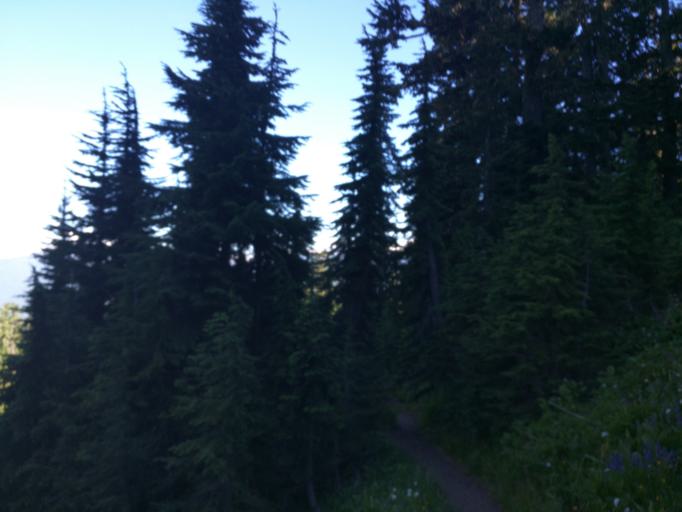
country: CA
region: British Columbia
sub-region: Fraser Valley Regional District
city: Chilliwack
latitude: 48.9263
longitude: -121.8676
